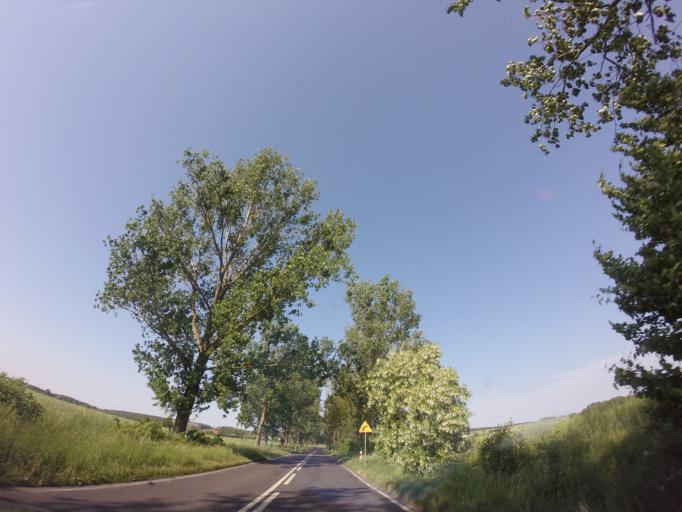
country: PL
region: West Pomeranian Voivodeship
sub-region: Powiat stargardzki
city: Kobylanka
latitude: 53.3183
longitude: 14.8492
